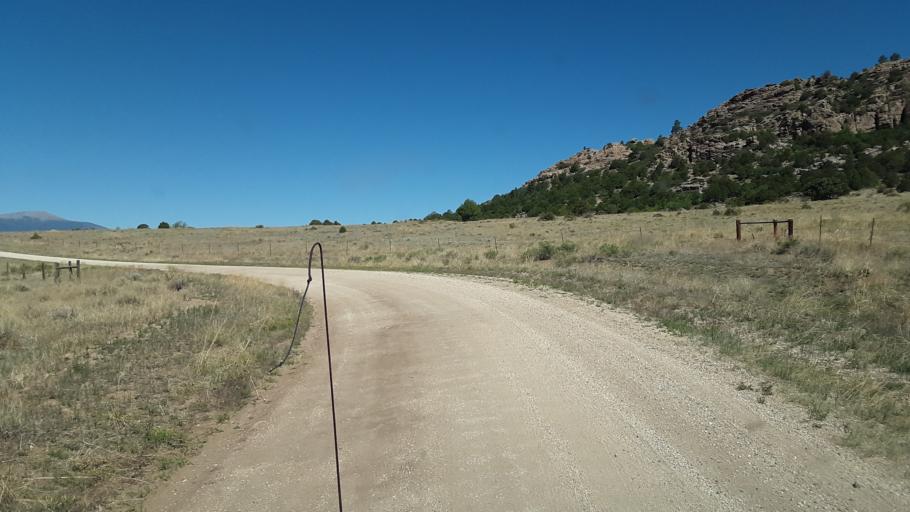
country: US
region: Colorado
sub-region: Custer County
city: Westcliffe
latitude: 38.2347
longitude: -105.4602
